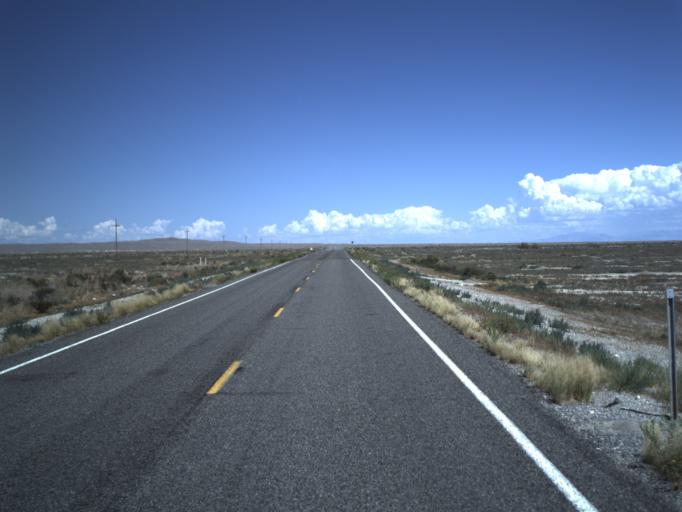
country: US
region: Utah
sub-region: Millard County
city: Delta
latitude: 39.0955
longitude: -113.1627
